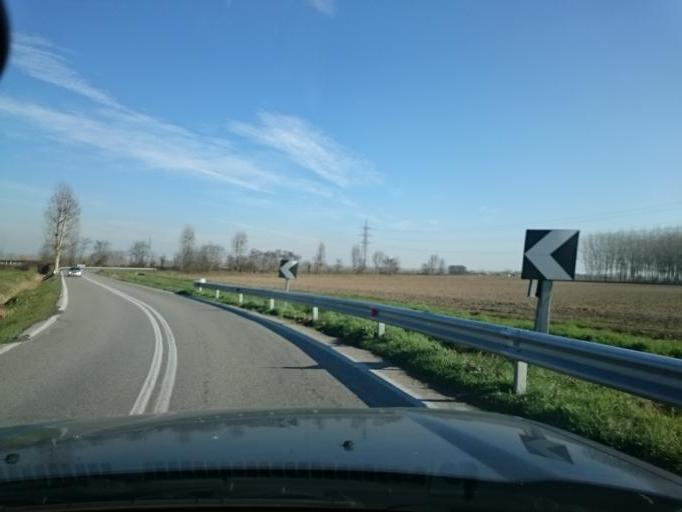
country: IT
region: Veneto
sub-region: Provincia di Verona
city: Vigasio
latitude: 45.2902
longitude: 10.9666
